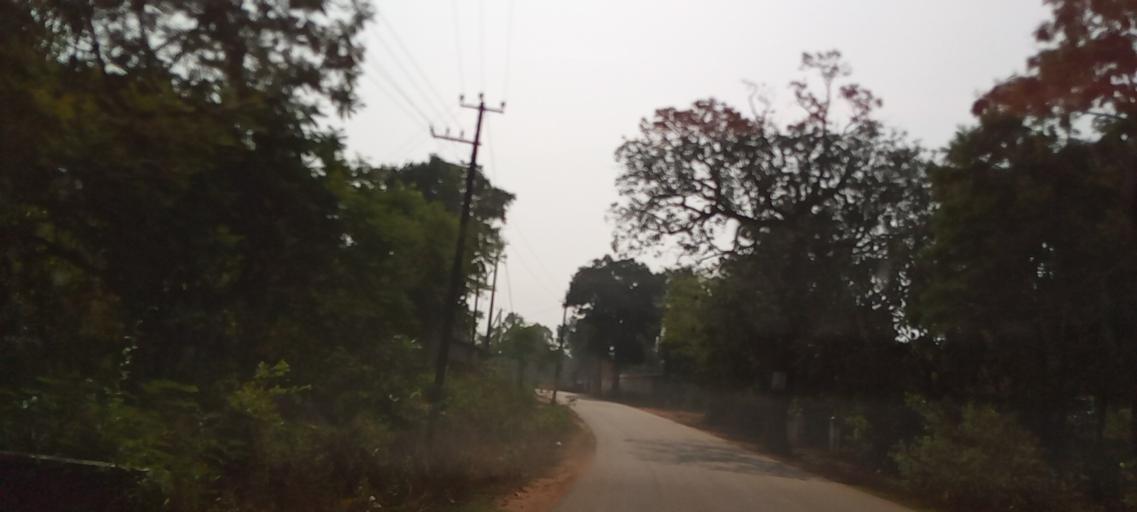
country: IN
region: Karnataka
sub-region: Udupi
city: Someshwar
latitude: 13.5211
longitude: 74.9295
